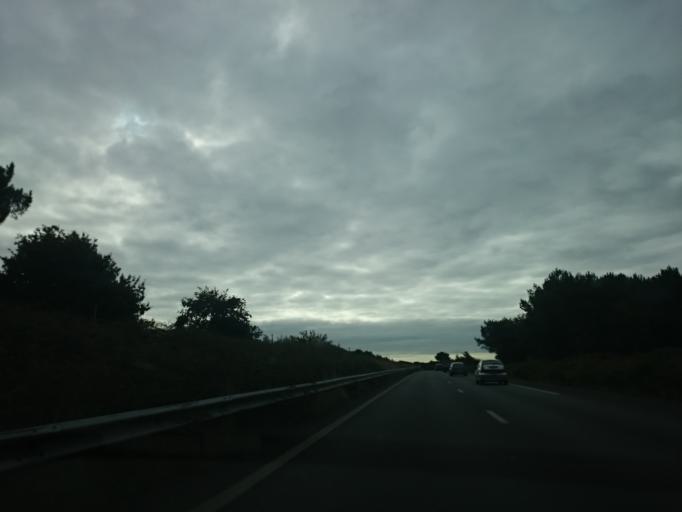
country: FR
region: Brittany
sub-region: Departement du Morbihan
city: Landaul
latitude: 47.7350
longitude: -3.0940
